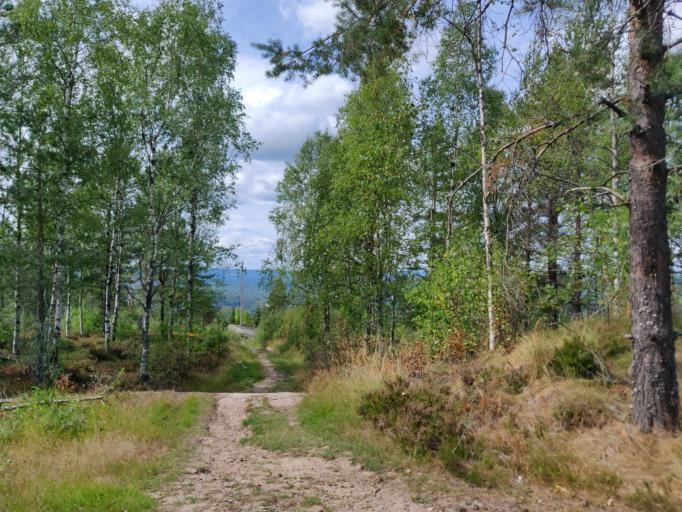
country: SE
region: Vaermland
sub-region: Hagfors Kommun
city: Hagfors
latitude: 60.0219
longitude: 13.7307
